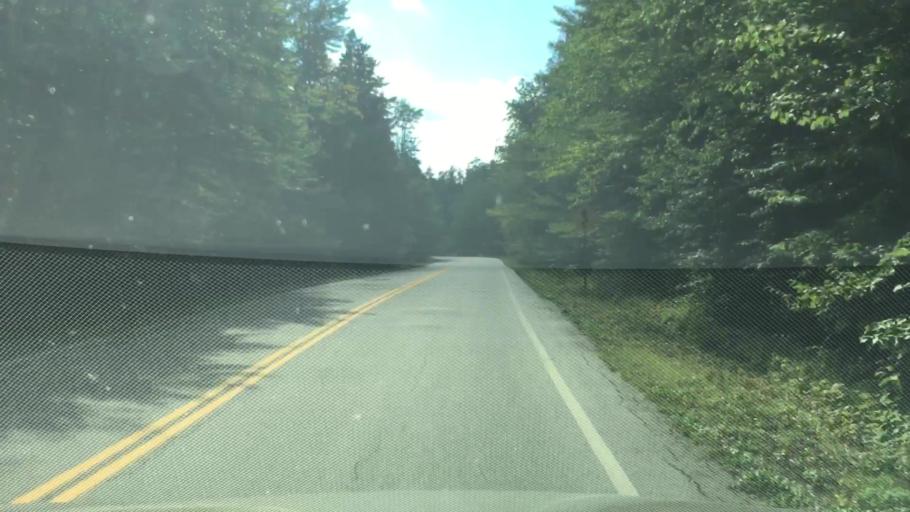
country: US
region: New Hampshire
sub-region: Carroll County
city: North Conway
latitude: 44.0437
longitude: -71.3140
